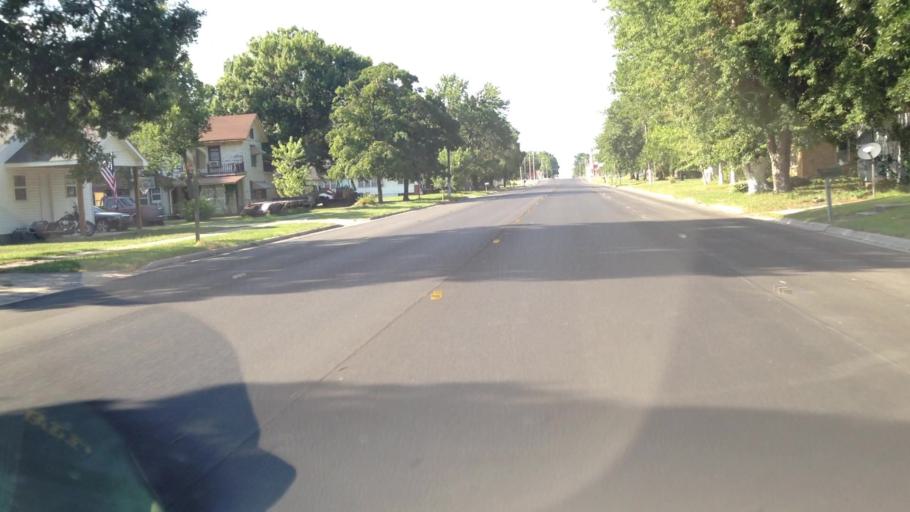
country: US
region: Kansas
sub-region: Allen County
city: Iola
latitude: 37.9114
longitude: -95.1701
